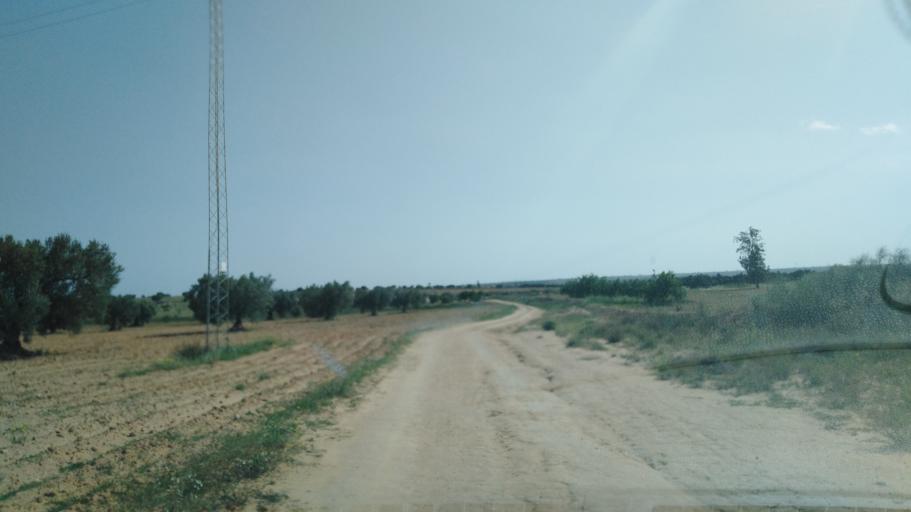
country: TN
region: Safaqis
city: Bi'r `Ali Bin Khalifah
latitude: 34.7907
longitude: 10.3711
